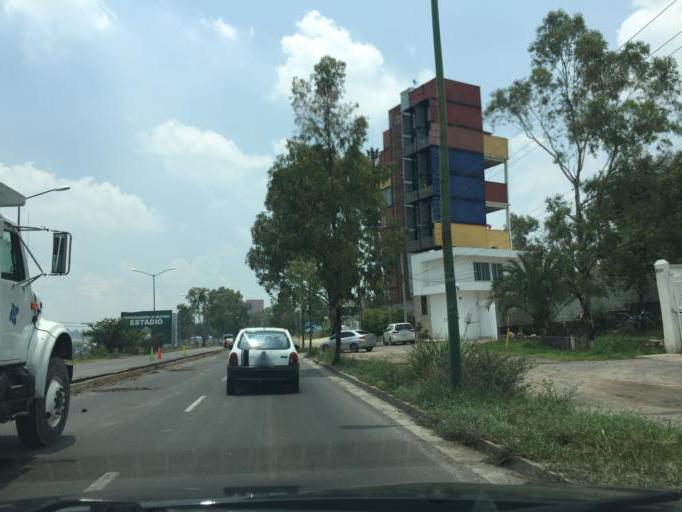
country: MX
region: Guanajuato
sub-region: Leon
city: La Ermita
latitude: 21.1650
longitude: -101.7275
